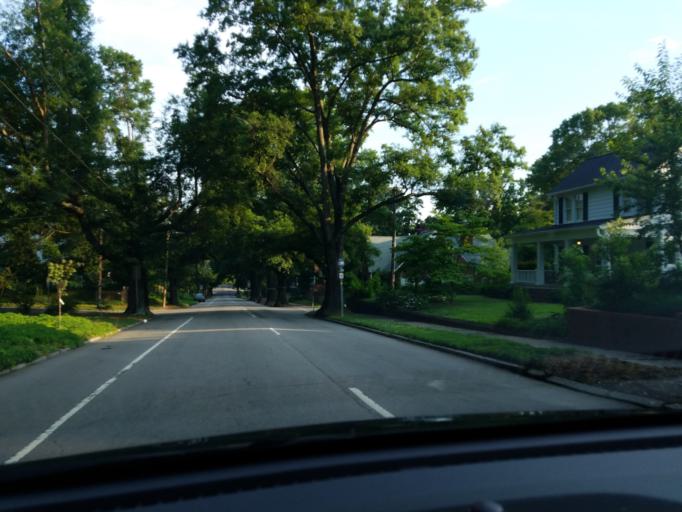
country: US
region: North Carolina
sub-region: Durham County
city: Durham
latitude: 36.0154
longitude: -78.9083
